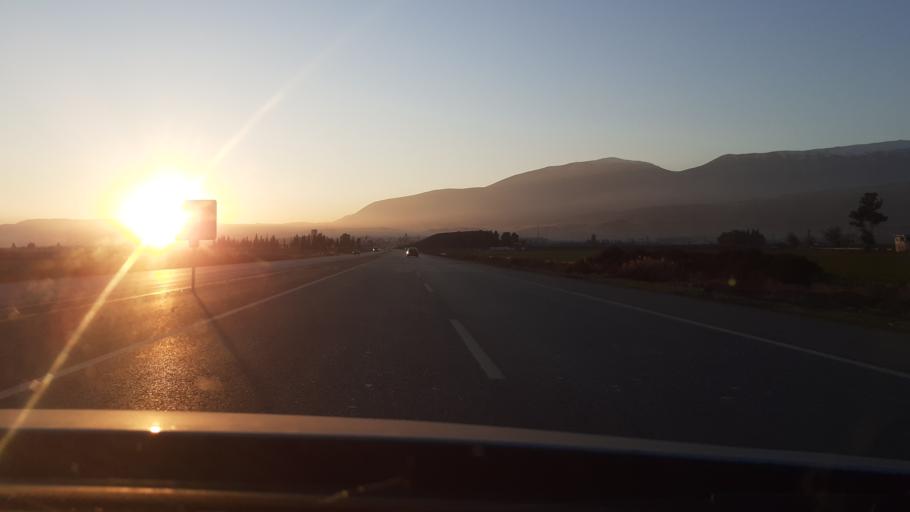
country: TR
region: Hatay
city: Kirikhan
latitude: 36.5037
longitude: 36.4027
